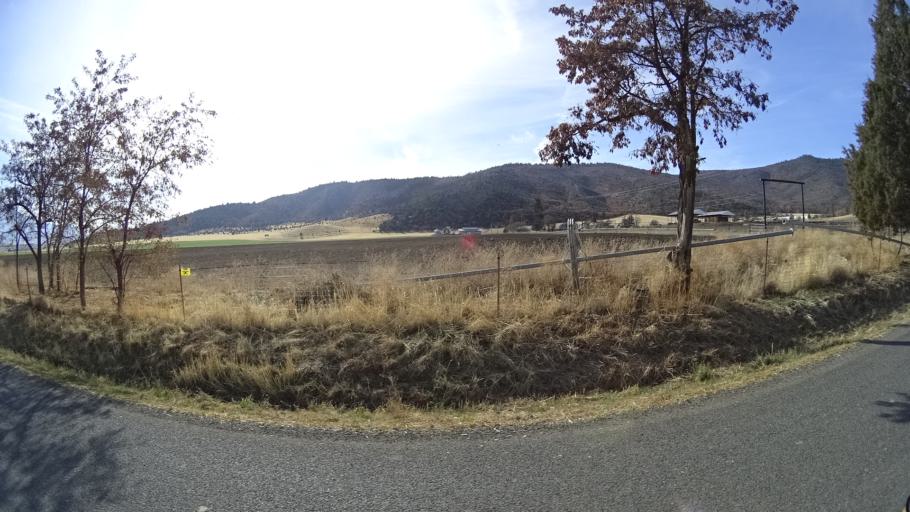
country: US
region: California
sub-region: Siskiyou County
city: Montague
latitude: 41.5382
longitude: -122.5596
